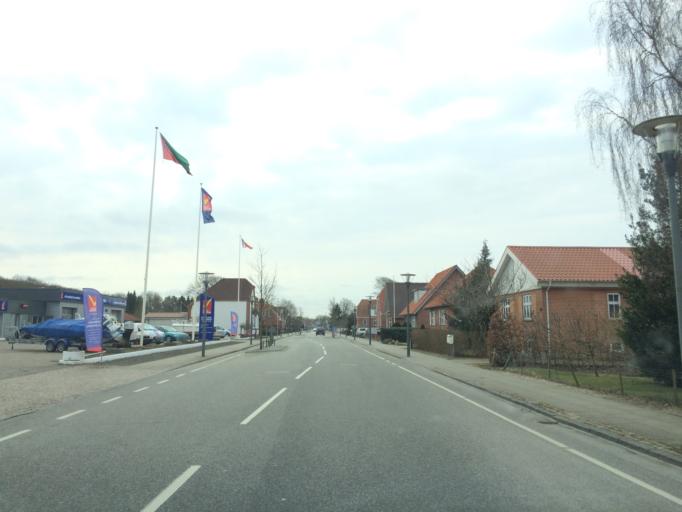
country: DK
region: Central Jutland
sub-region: Ringkobing-Skjern Kommune
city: Tarm
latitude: 55.9137
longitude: 8.5194
